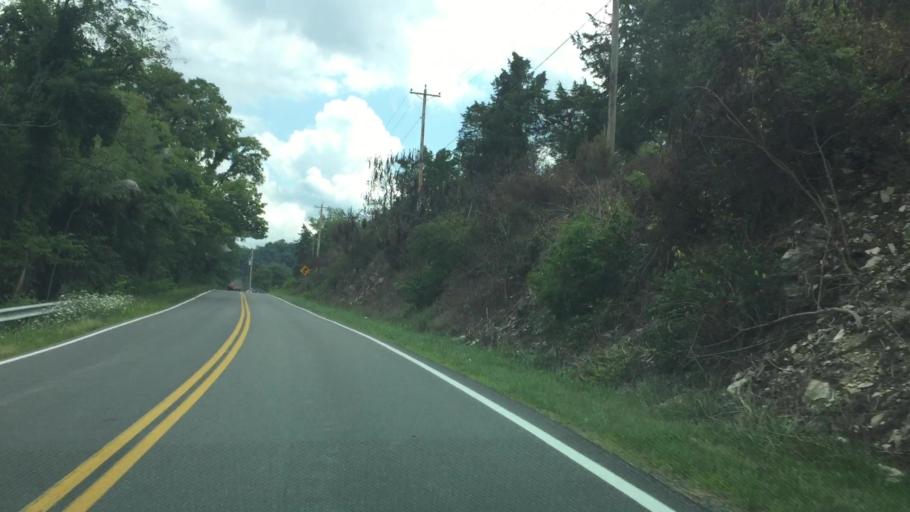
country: US
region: Virginia
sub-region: Pulaski County
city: Dublin
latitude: 37.0492
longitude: -80.7118
